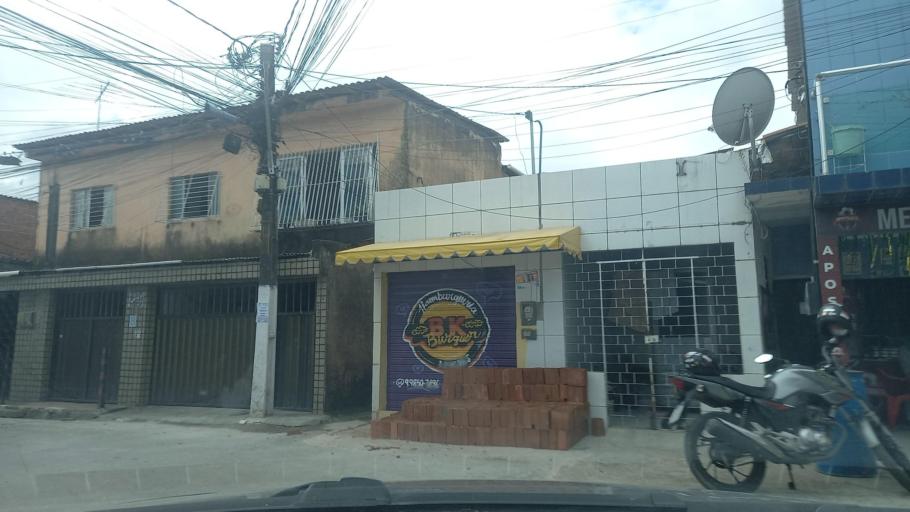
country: BR
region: Pernambuco
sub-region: Recife
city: Recife
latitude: -8.1048
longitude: -34.9187
